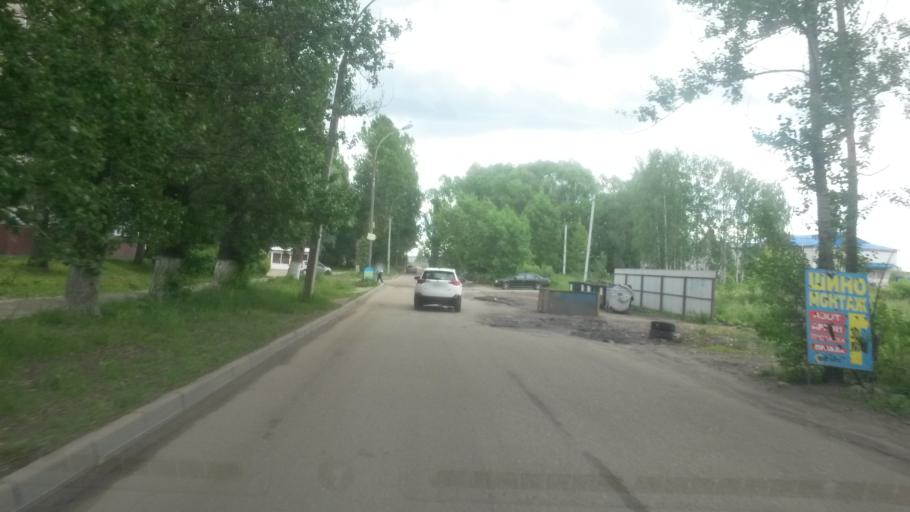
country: RU
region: Jaroslavl
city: Yaroslavl
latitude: 57.6740
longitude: 39.7750
